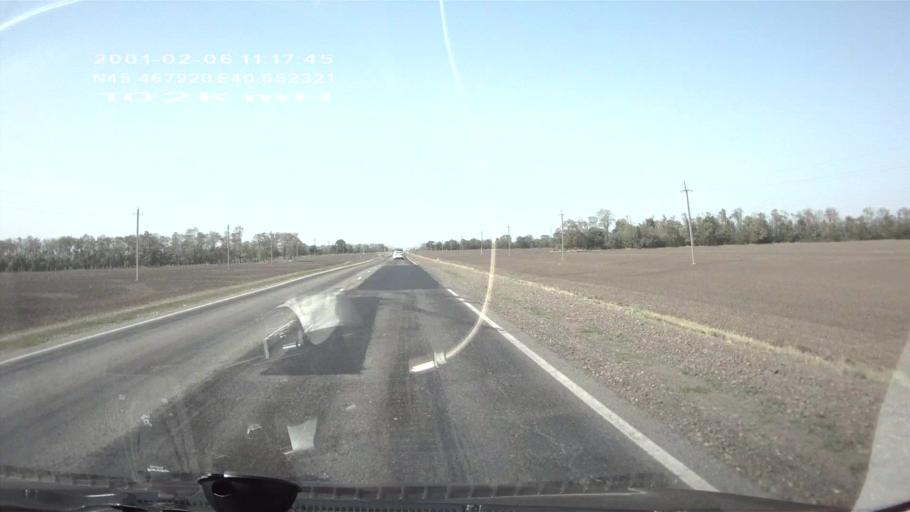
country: RU
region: Krasnodarskiy
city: Kavkazskaya
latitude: 45.4682
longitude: 40.6527
